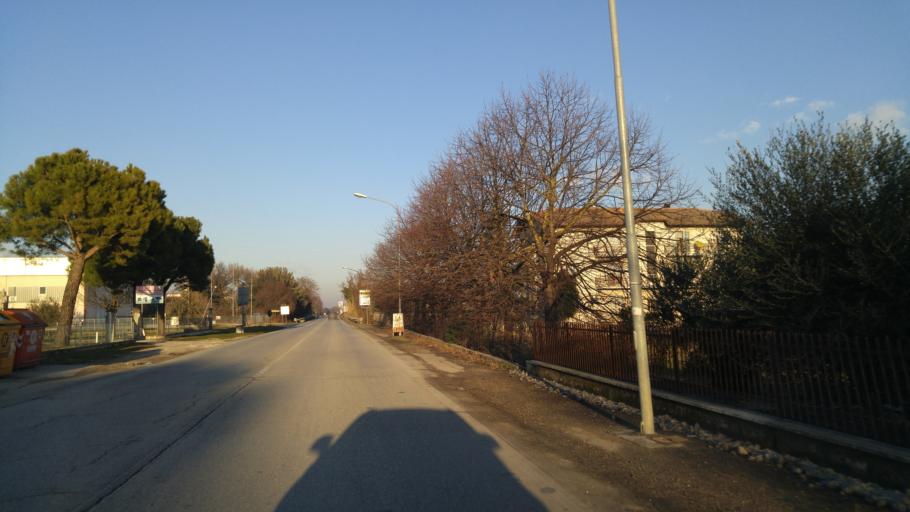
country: IT
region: The Marches
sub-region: Provincia di Pesaro e Urbino
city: Monte Porzio
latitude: 43.7006
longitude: 13.0630
